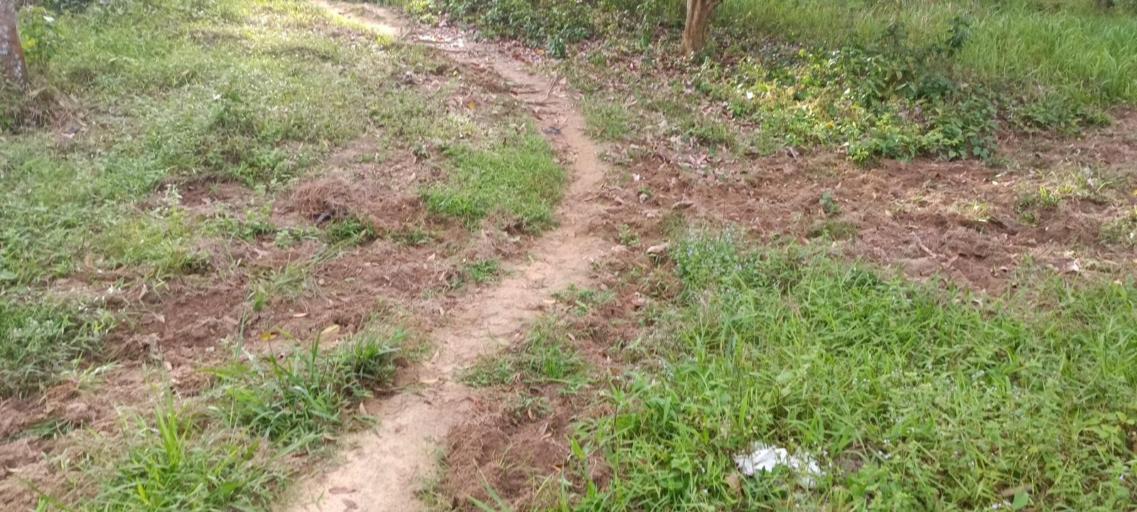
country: MY
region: Penang
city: Nibong Tebal
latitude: 5.2308
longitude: 100.5130
